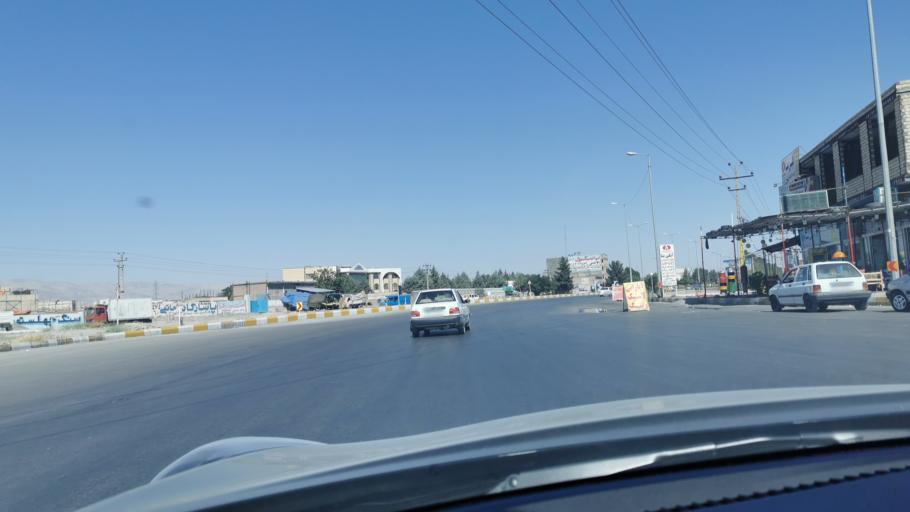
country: IR
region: Razavi Khorasan
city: Chenaran
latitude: 36.6347
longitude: 59.1300
